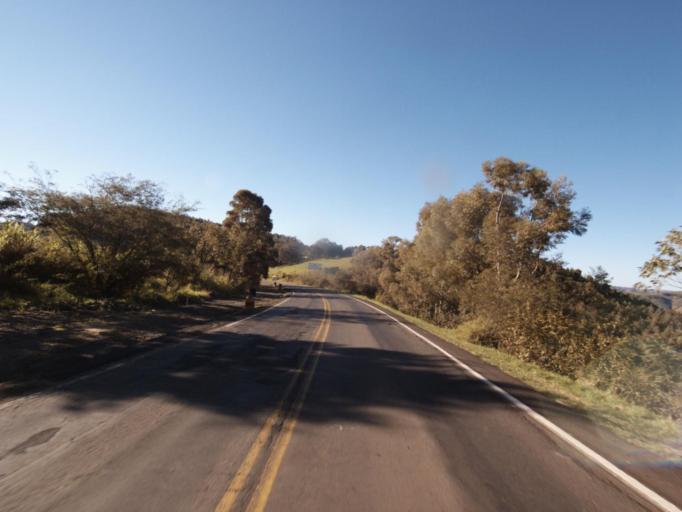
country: AR
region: Misiones
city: Bernardo de Irigoyen
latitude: -26.4856
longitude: -53.5035
